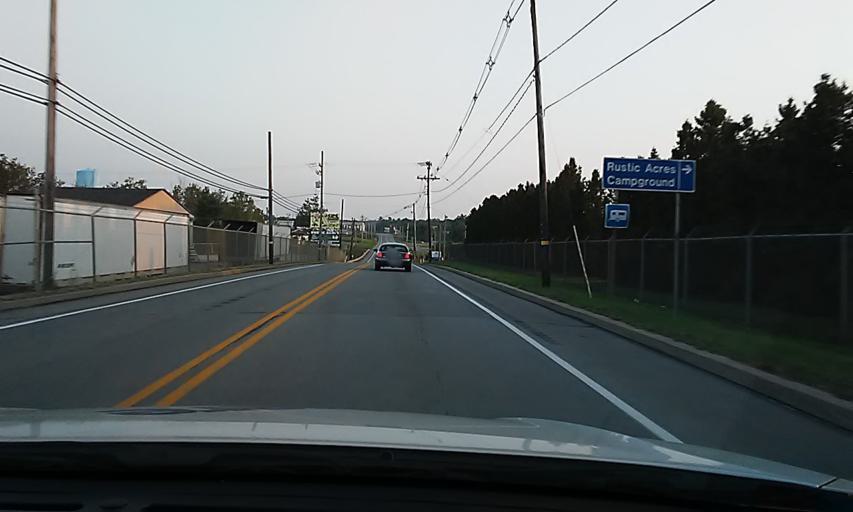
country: US
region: Pennsylvania
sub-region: Clarion County
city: Marianne
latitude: 41.2390
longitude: -79.4283
